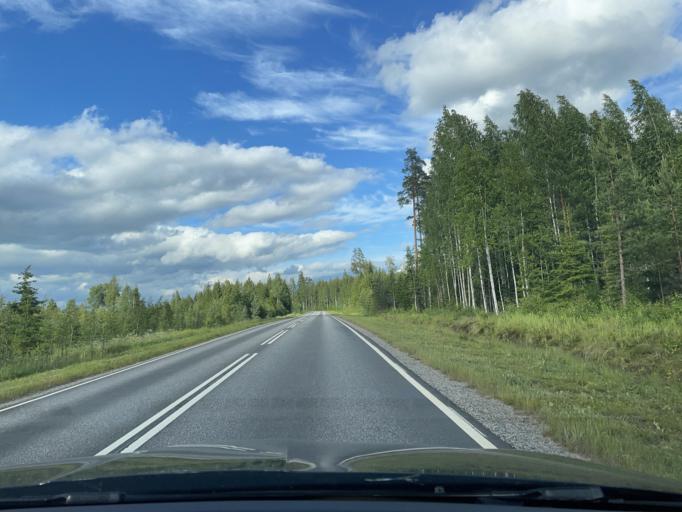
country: FI
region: Central Finland
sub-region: Jyvaeskylae
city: Petaejaevesi
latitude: 62.0926
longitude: 25.1556
